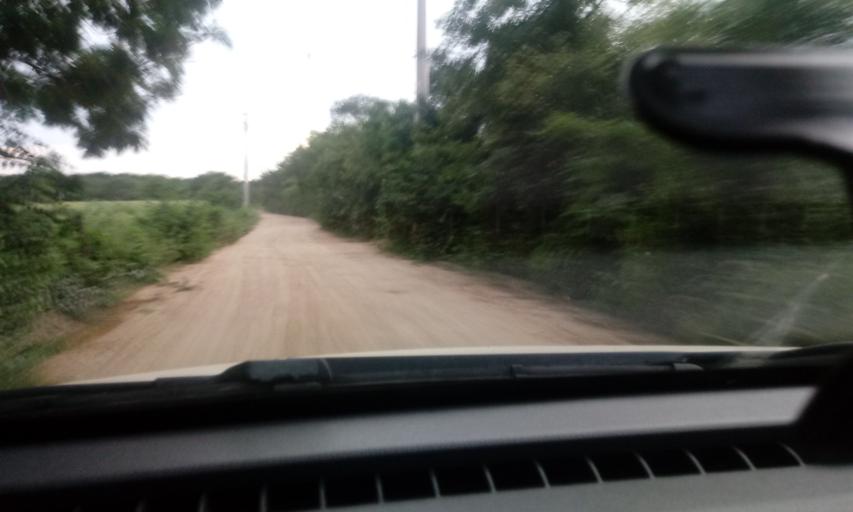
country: BR
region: Bahia
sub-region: Riacho De Santana
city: Riacho de Santana
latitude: -13.8028
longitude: -42.7538
